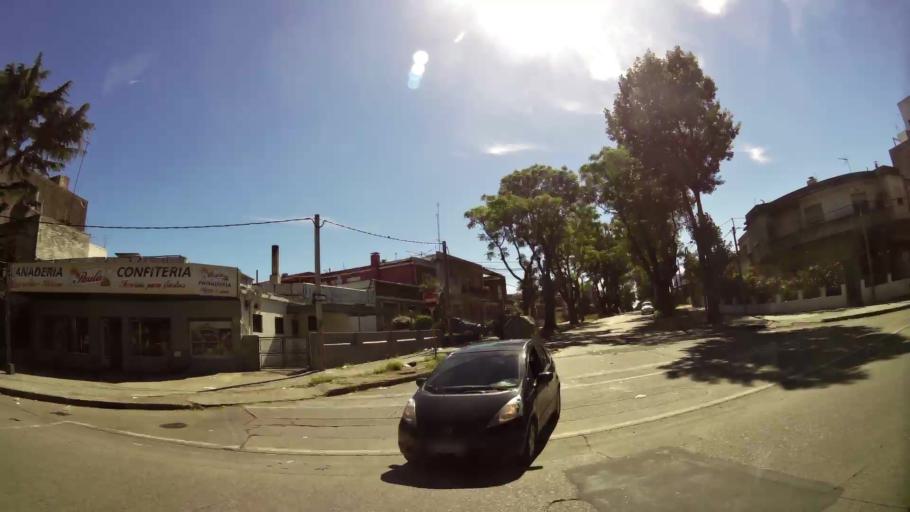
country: UY
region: Montevideo
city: Montevideo
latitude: -34.8890
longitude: -56.1277
